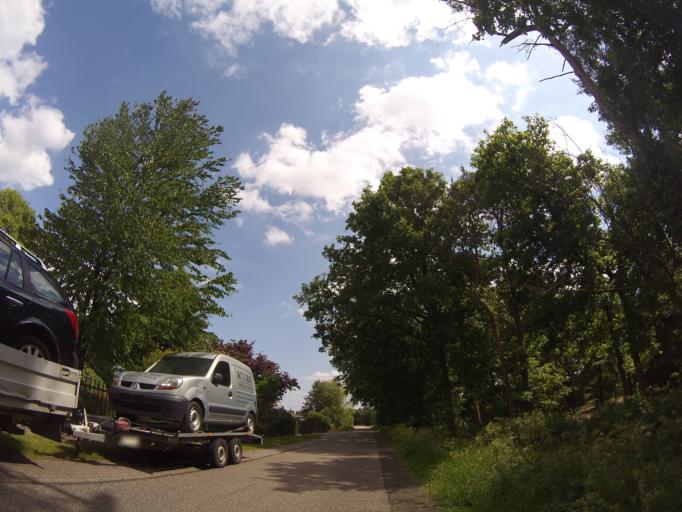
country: NL
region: Gelderland
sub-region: Gemeente Barneveld
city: Voorthuizen
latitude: 52.1957
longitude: 5.6246
